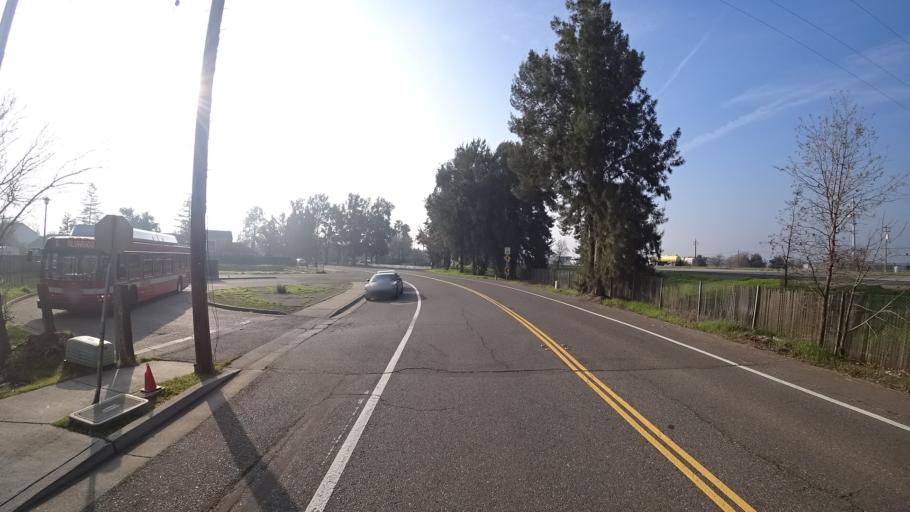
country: US
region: California
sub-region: Yolo County
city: Davis
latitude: 38.5683
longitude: -121.7672
